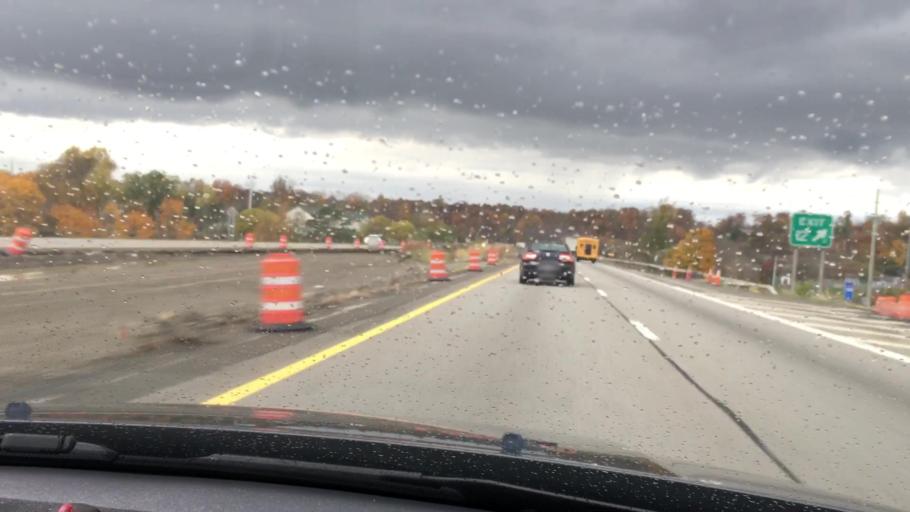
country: US
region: New York
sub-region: Dutchess County
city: Fishkill
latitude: 41.5262
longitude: -73.9141
